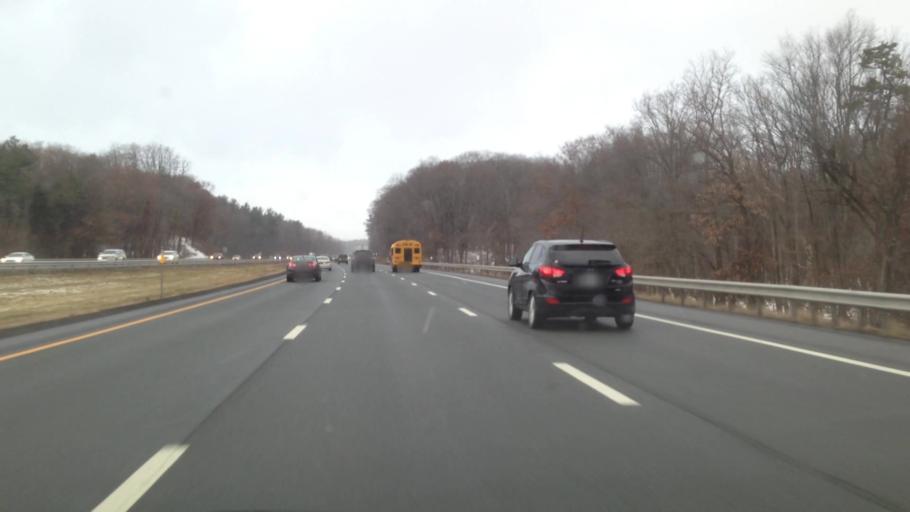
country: US
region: New York
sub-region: Albany County
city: Westmere
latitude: 42.7353
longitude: -73.9020
